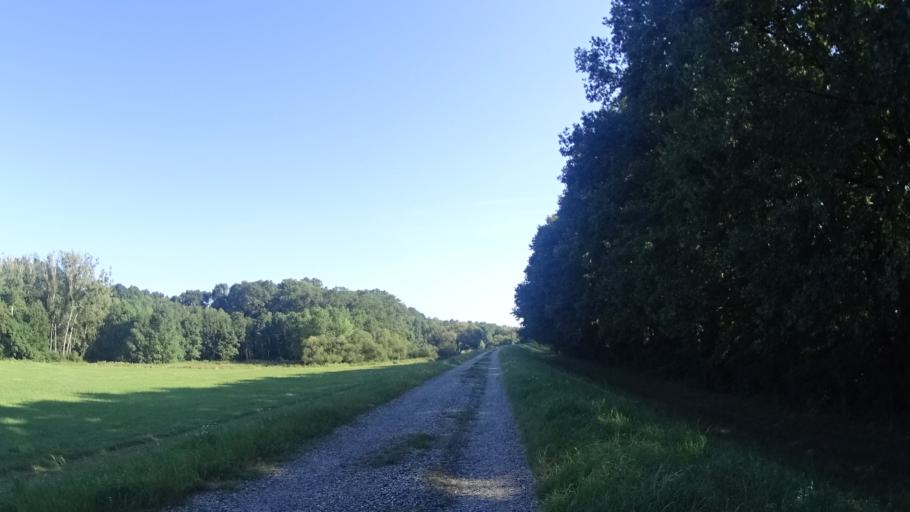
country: CZ
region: South Moravian
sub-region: Okres Breclav
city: Lanzhot
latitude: 48.6604
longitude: 16.9783
